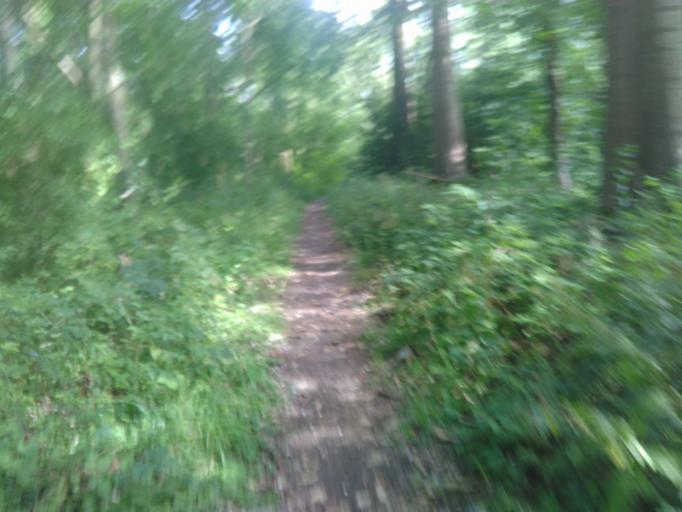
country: BE
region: Flanders
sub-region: Provincie Vlaams-Brabant
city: Oud-Heverlee
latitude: 50.8544
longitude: 4.6662
